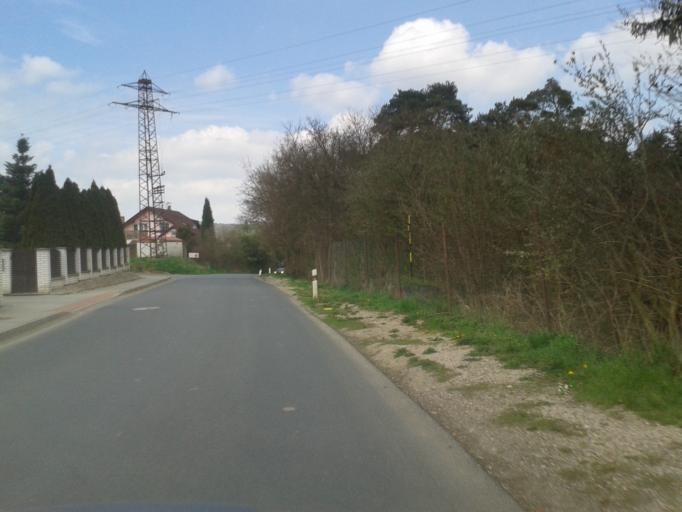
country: CZ
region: Central Bohemia
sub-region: Okres Beroun
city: Lodenice
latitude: 50.0081
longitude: 14.1518
